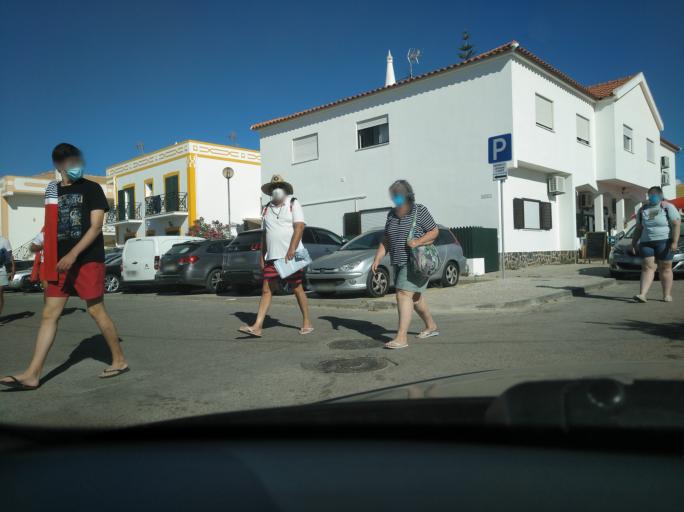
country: PT
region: Faro
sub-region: Vila Real de Santo Antonio
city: Monte Gordo
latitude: 37.1689
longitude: -7.5126
